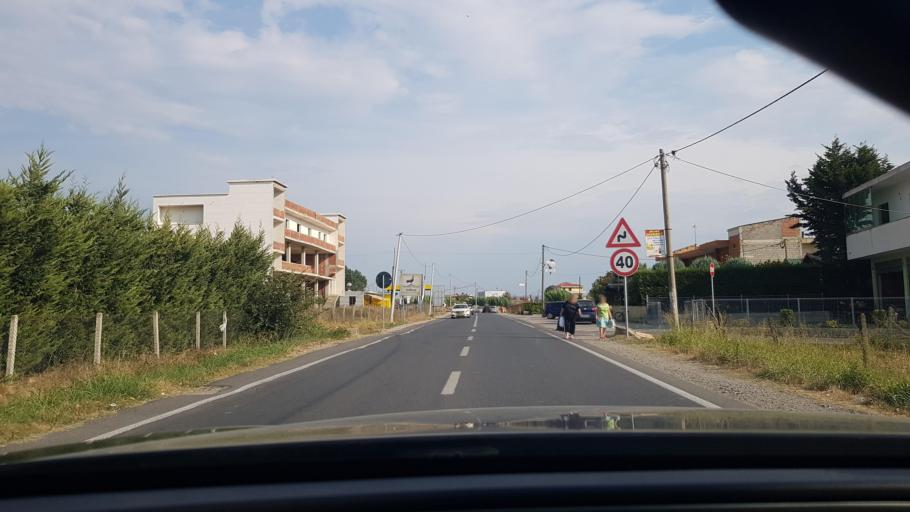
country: AL
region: Durres
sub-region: Rrethi i Durresit
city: Manze
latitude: 41.4493
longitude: 19.5714
